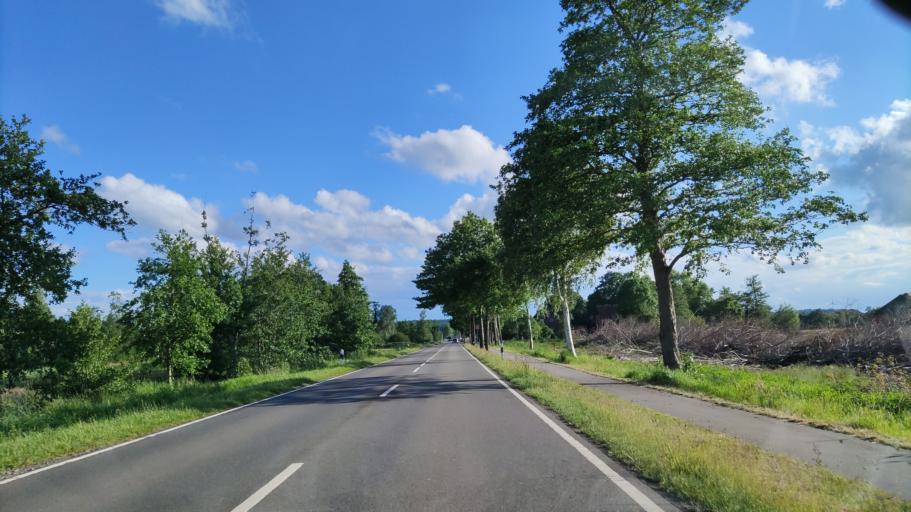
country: DE
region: Lower Saxony
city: Buxtehude
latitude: 53.4963
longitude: 9.6553
